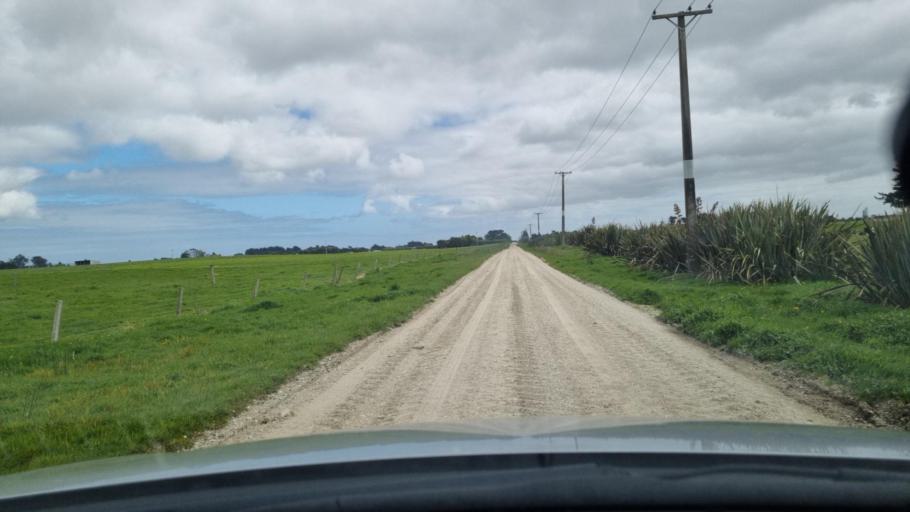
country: NZ
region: Southland
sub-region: Invercargill City
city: Invercargill
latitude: -46.4433
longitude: 168.4200
